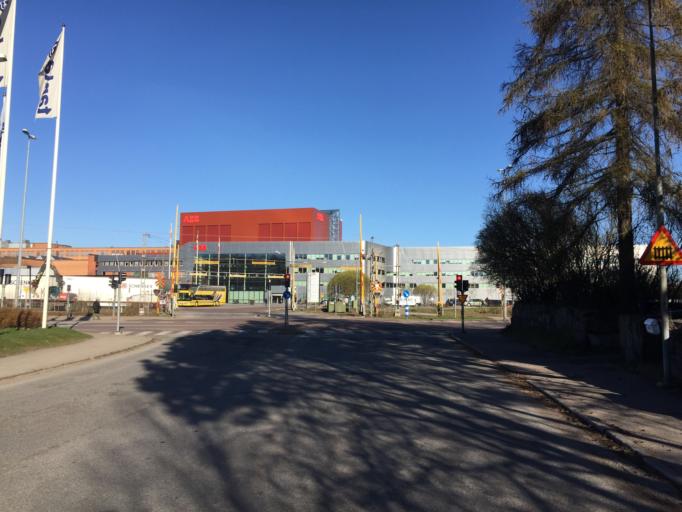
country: SE
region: Dalarna
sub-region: Ludvika Kommun
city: Ludvika
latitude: 60.1446
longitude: 15.1802
